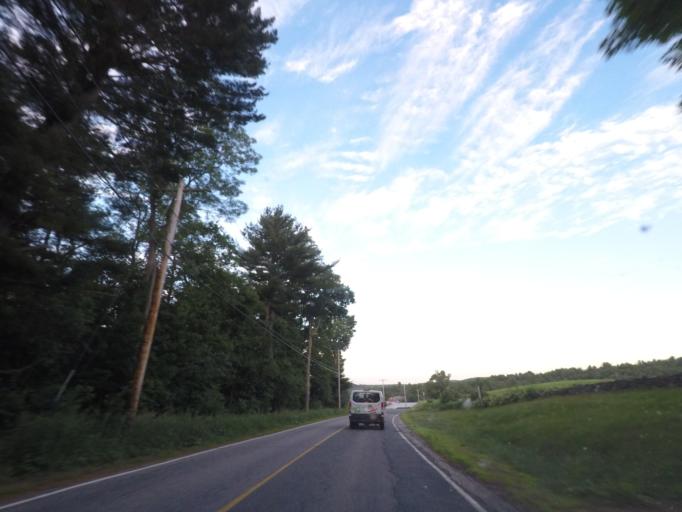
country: US
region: Massachusetts
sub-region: Worcester County
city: Fiskdale
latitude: 42.1611
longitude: -72.1460
